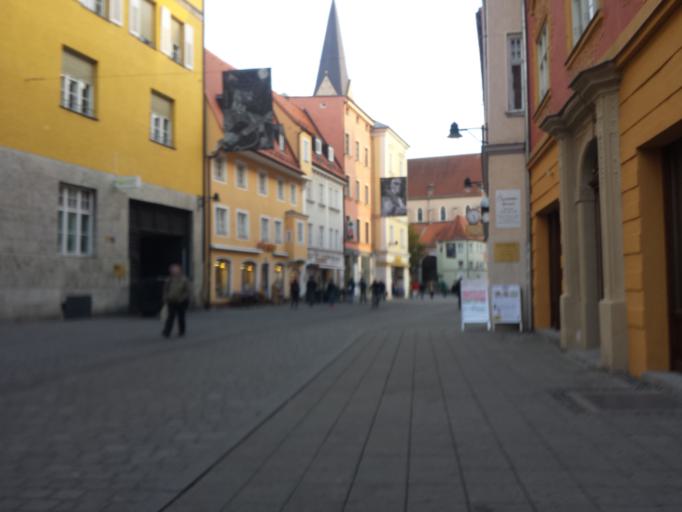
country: DE
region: Bavaria
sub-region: Upper Bavaria
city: Ingolstadt
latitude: 48.7647
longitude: 11.4239
